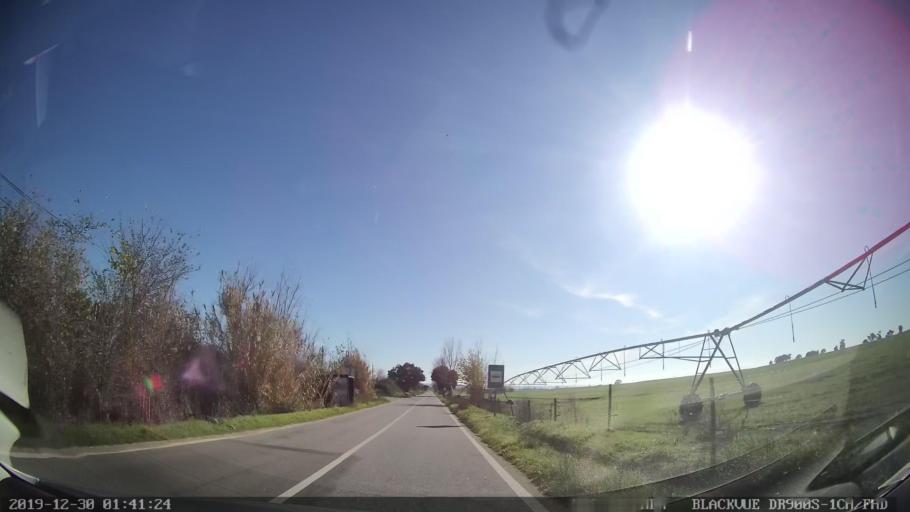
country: PT
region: Castelo Branco
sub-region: Idanha-A-Nova
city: Idanha-a-Nova
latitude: 39.8725
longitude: -7.1877
